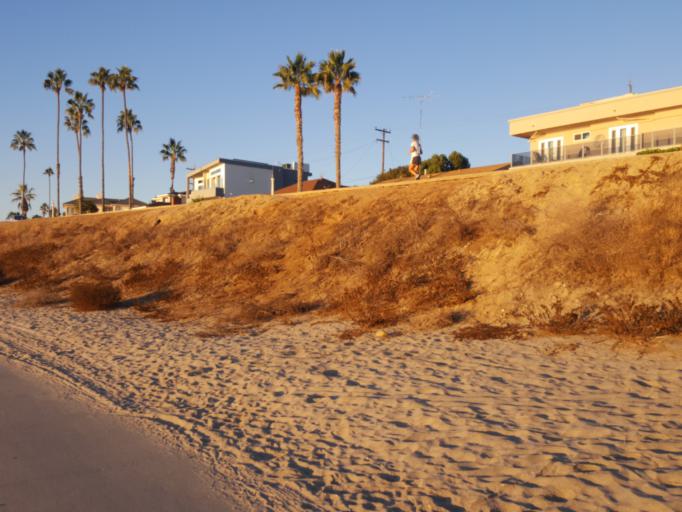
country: US
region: California
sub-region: San Diego County
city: La Jolla
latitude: 32.7819
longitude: -117.2343
